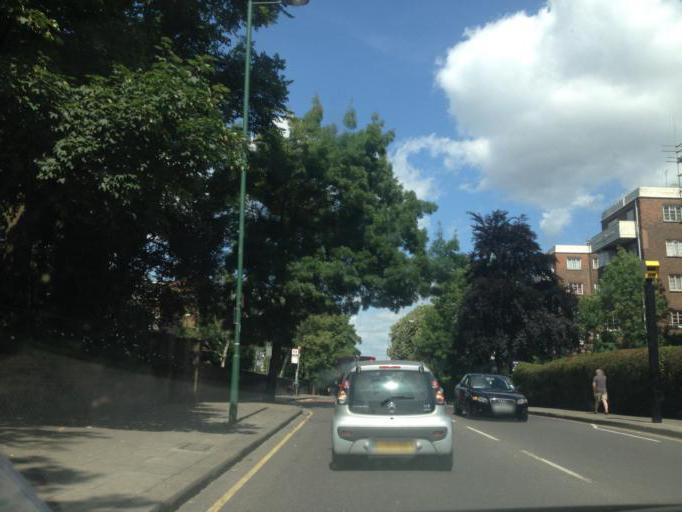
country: GB
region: England
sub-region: Greater London
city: Belsize Park
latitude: 51.5502
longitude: -0.2073
